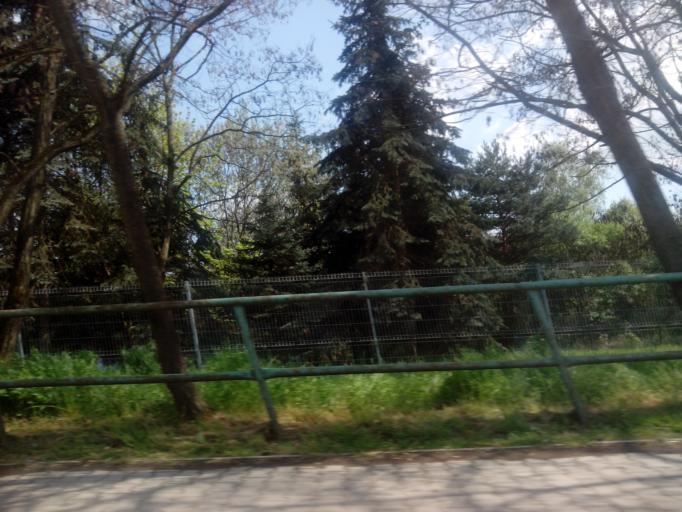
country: CZ
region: Central Bohemia
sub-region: Okres Beroun
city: Lodenice
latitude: 49.9918
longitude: 14.1532
